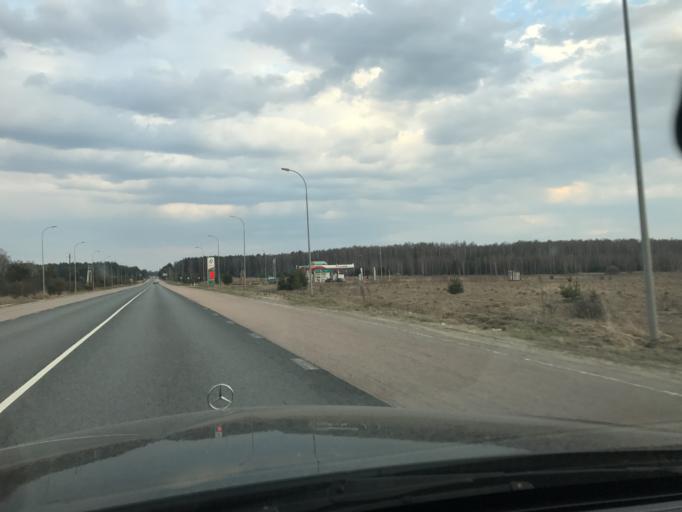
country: RU
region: Vladimir
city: Murom
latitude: 55.6240
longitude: 41.8981
